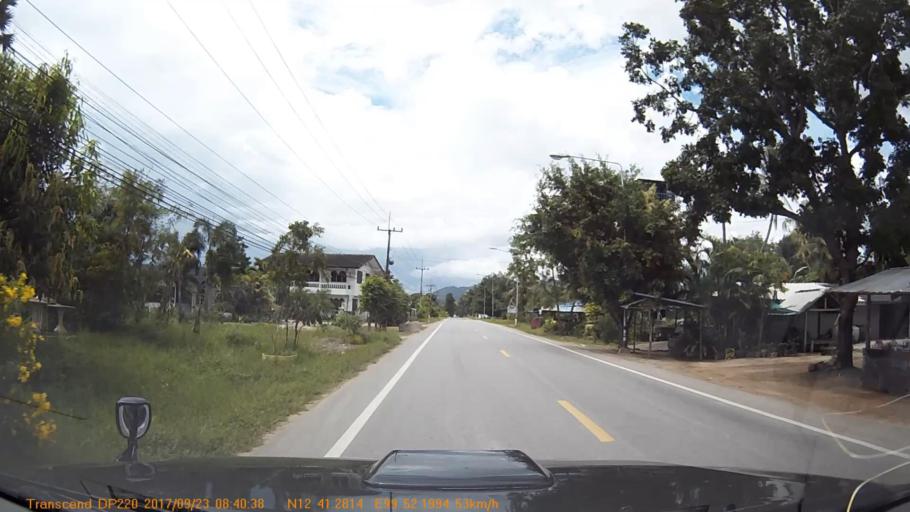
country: TH
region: Prachuap Khiri Khan
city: Hua Hin
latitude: 12.6881
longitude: 99.8700
